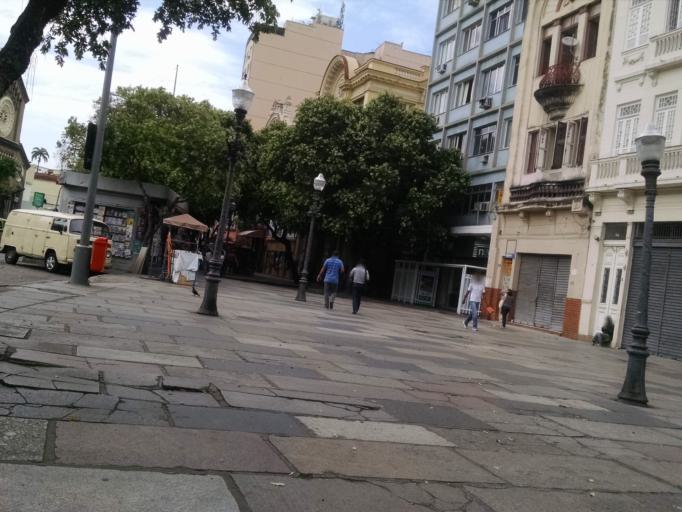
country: BR
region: Rio de Janeiro
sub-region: Rio De Janeiro
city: Rio de Janeiro
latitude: -22.9238
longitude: -43.1772
